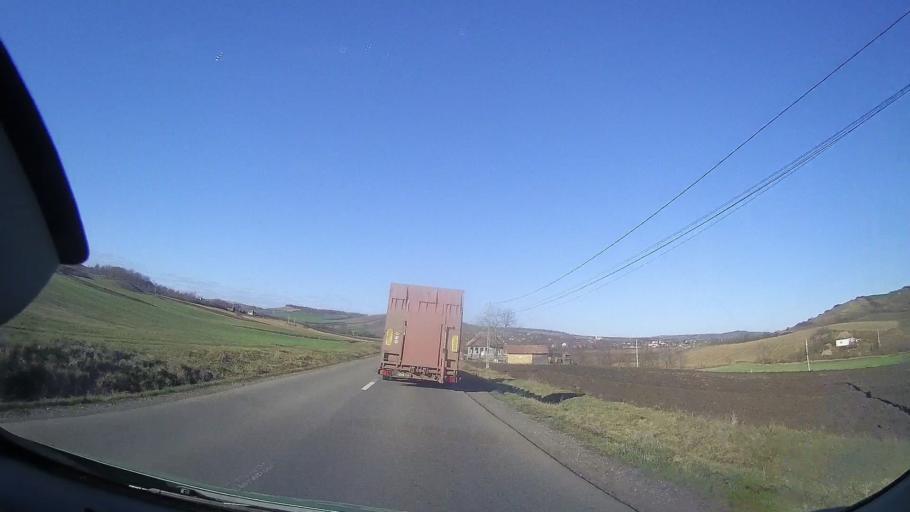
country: RO
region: Mures
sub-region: Comuna Sarmasu
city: Balda
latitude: 46.7180
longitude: 24.1472
